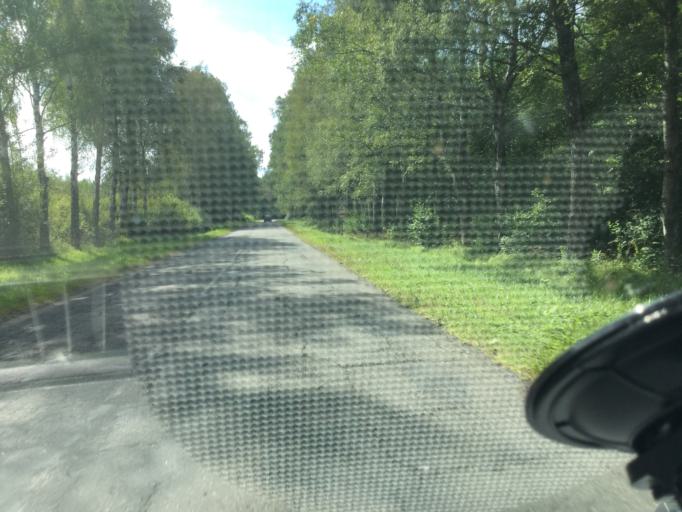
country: BY
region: Vitebsk
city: Chashniki
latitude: 55.3025
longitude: 29.3931
